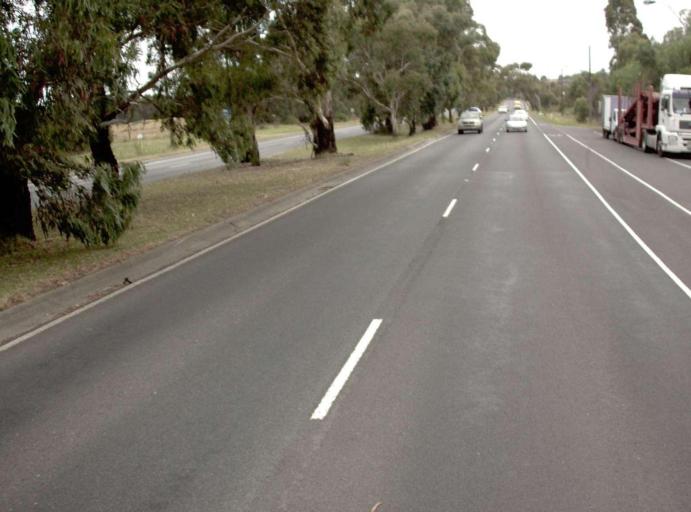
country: AU
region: Victoria
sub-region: Knox
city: Rowville
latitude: -37.9460
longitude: 145.2293
